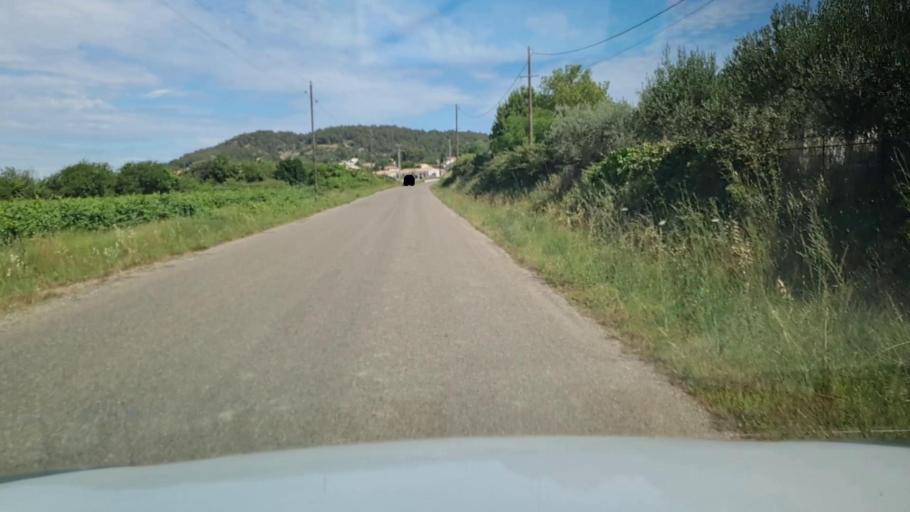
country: FR
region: Languedoc-Roussillon
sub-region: Departement du Gard
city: Nages-et-Solorgues
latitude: 43.7849
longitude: 4.2327
